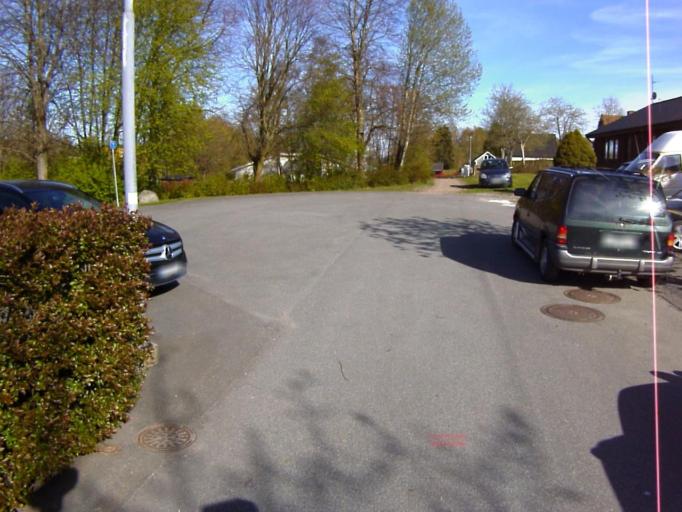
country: SE
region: Skane
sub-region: Kristianstads Kommun
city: Onnestad
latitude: 55.9954
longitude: 14.0344
